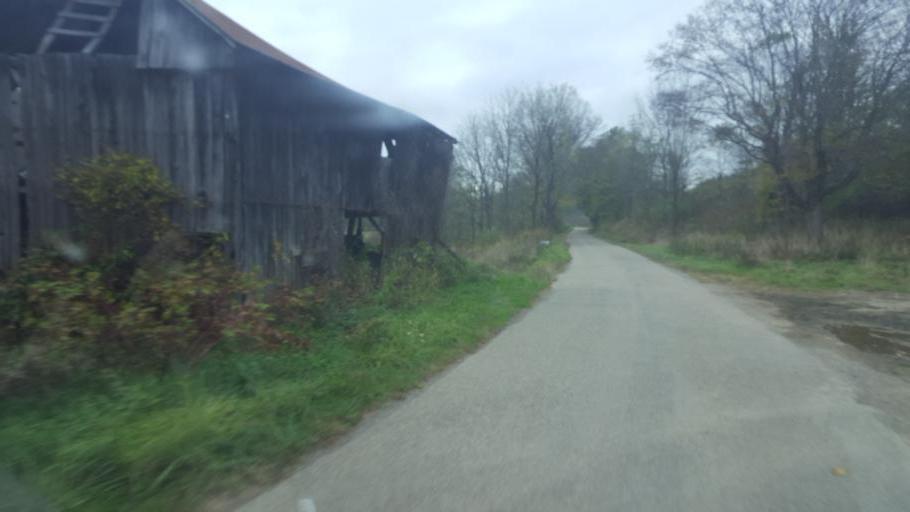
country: US
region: Ohio
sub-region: Harrison County
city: Cadiz
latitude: 40.4158
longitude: -81.0344
